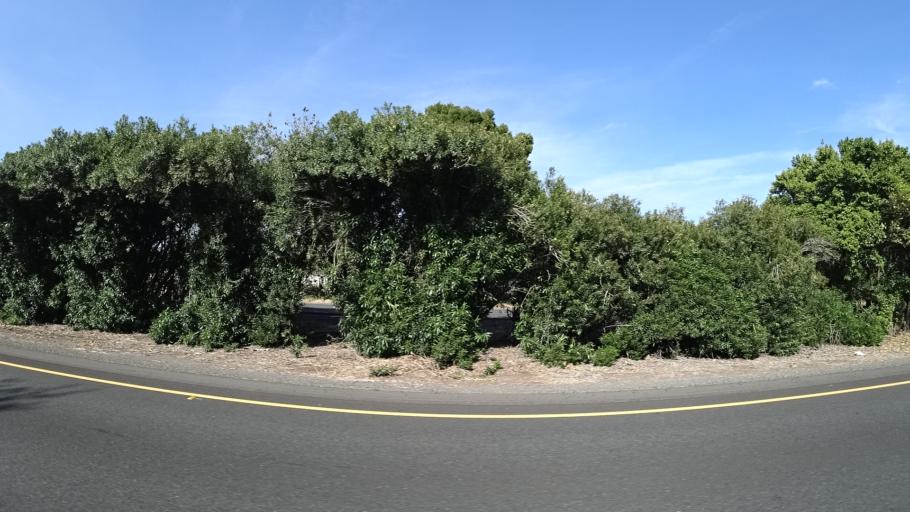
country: US
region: California
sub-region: Butte County
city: Chico
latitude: 39.7676
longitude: -121.8651
